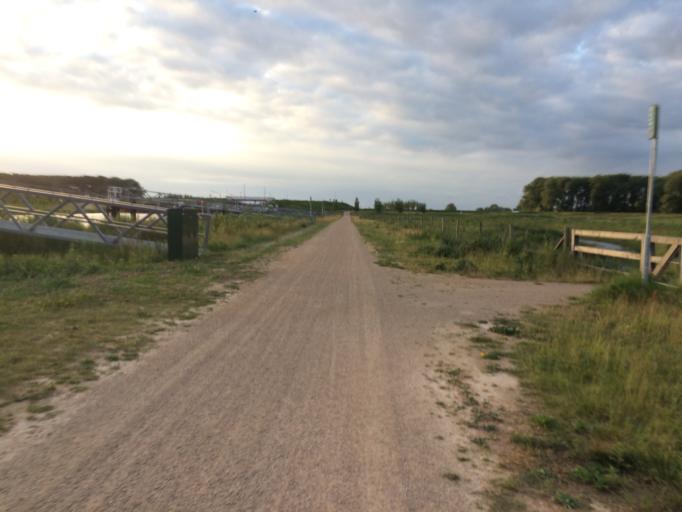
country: NL
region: North Brabant
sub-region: Gemeente 's-Hertogenbosch
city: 's-Hertogenbosch
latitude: 51.7364
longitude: 5.3367
